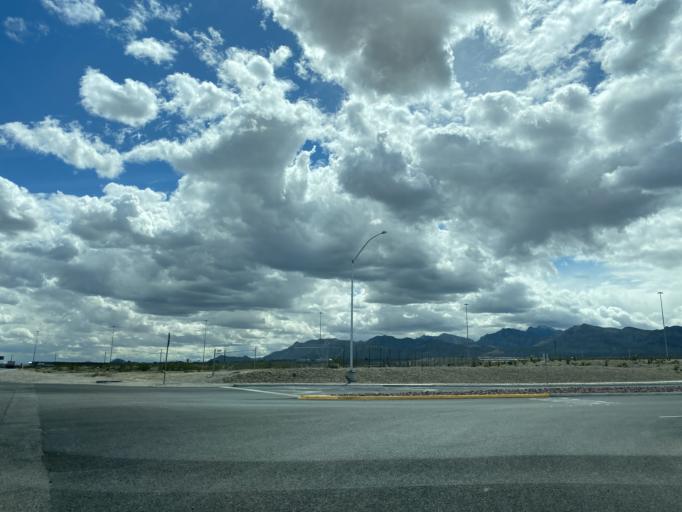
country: US
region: Nevada
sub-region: Clark County
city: Summerlin South
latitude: 36.3270
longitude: -115.3080
